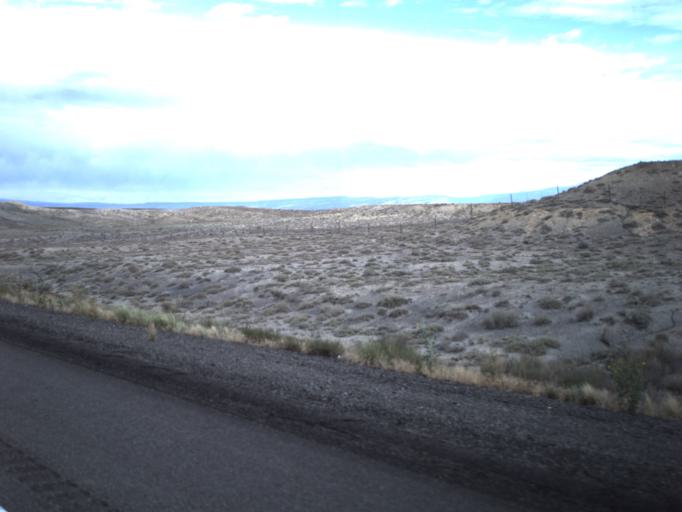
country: US
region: Utah
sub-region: Grand County
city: Moab
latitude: 38.9415
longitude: -109.5367
